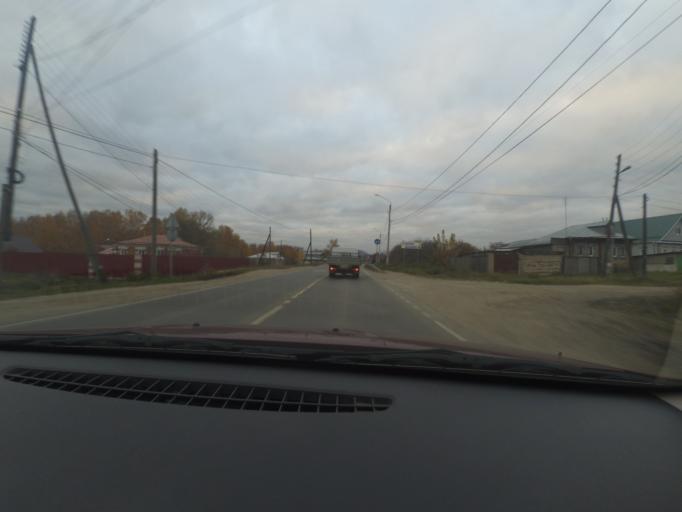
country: RU
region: Nizjnij Novgorod
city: Taremskoye
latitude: 55.9323
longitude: 43.0443
